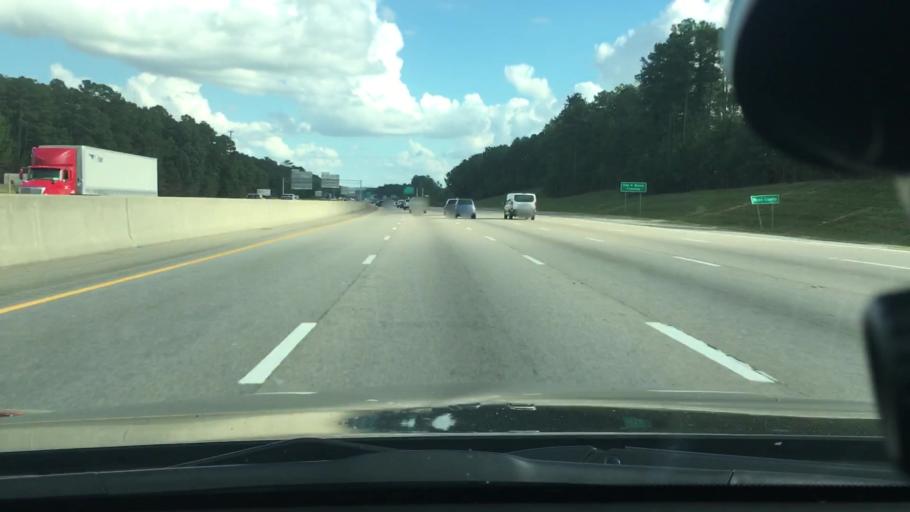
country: US
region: North Carolina
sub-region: Wake County
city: Morrisville
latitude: 35.8710
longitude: -78.8287
